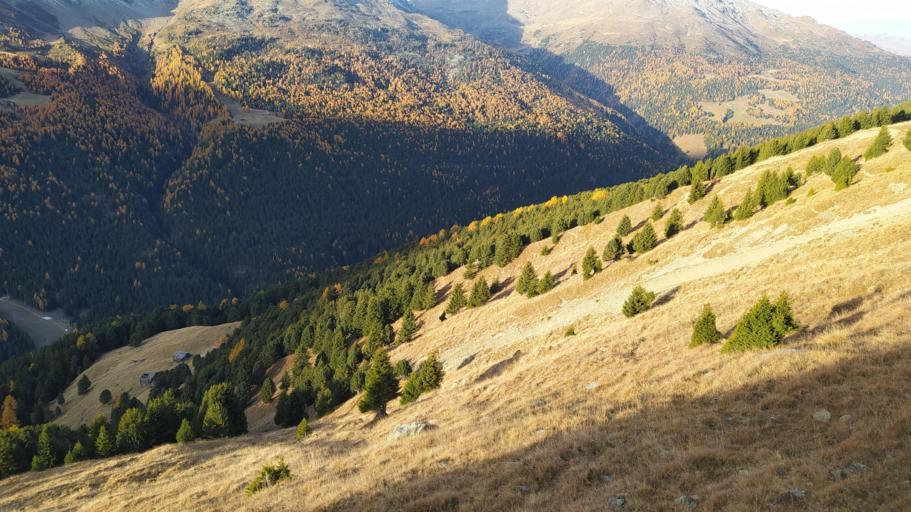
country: IT
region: Lombardy
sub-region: Provincia di Sondrio
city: Sant'Antonio
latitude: 46.4235
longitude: 10.4976
